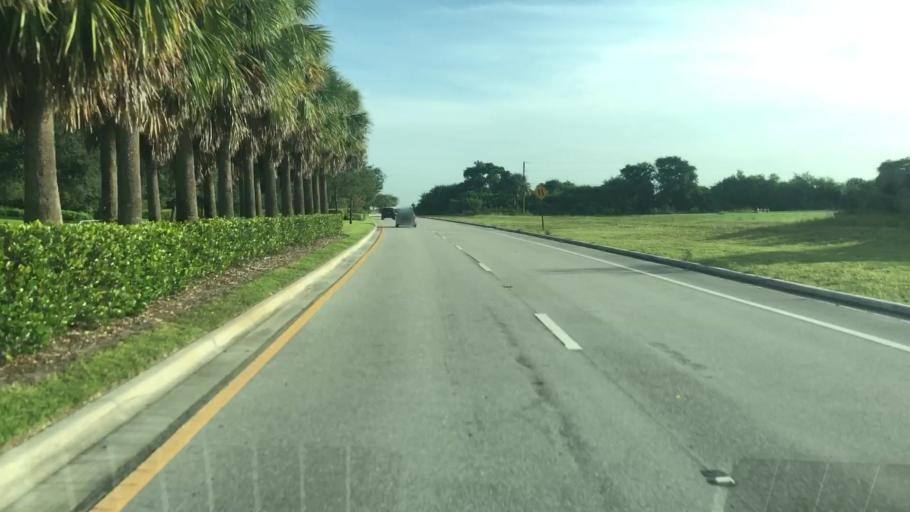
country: US
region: Florida
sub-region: Broward County
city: Parkland
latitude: 26.3185
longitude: -80.2510
